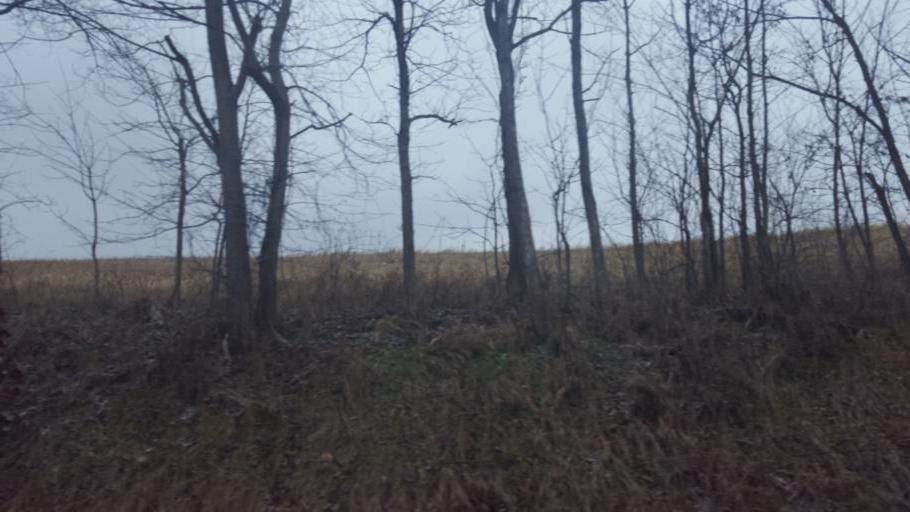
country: US
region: Ohio
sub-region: Coshocton County
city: West Lafayette
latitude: 40.3628
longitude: -81.7647
